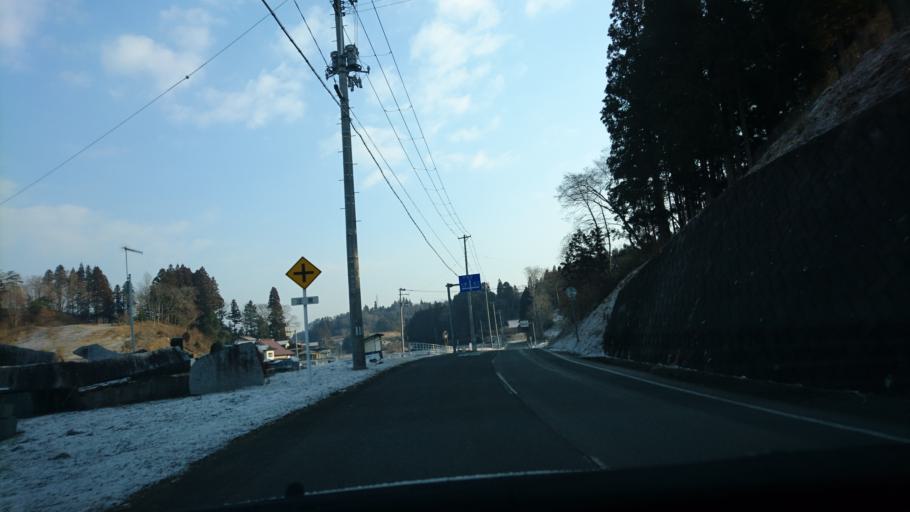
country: JP
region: Iwate
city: Ichinoseki
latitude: 38.9109
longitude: 141.3782
